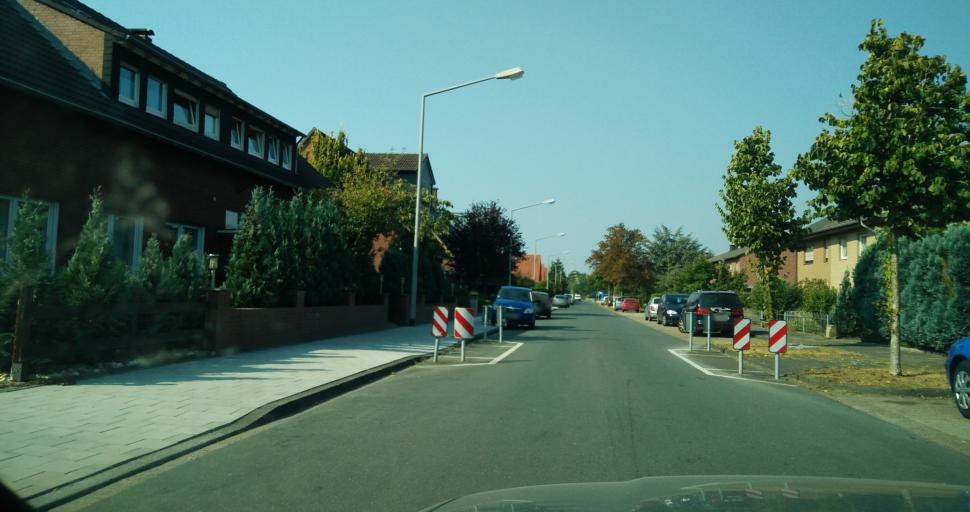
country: DE
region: North Rhine-Westphalia
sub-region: Regierungsbezirk Munster
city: Muenster
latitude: 51.9215
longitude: 7.6246
